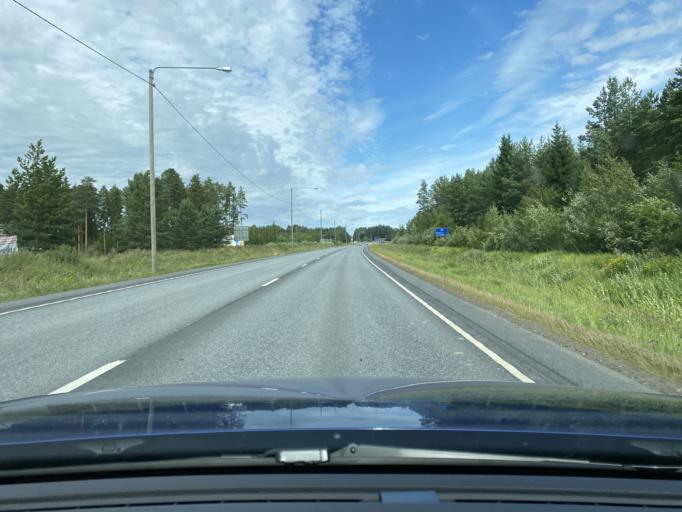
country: FI
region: Southern Ostrobothnia
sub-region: Seinaejoki
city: Ylihaermae
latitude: 63.1458
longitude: 22.8230
